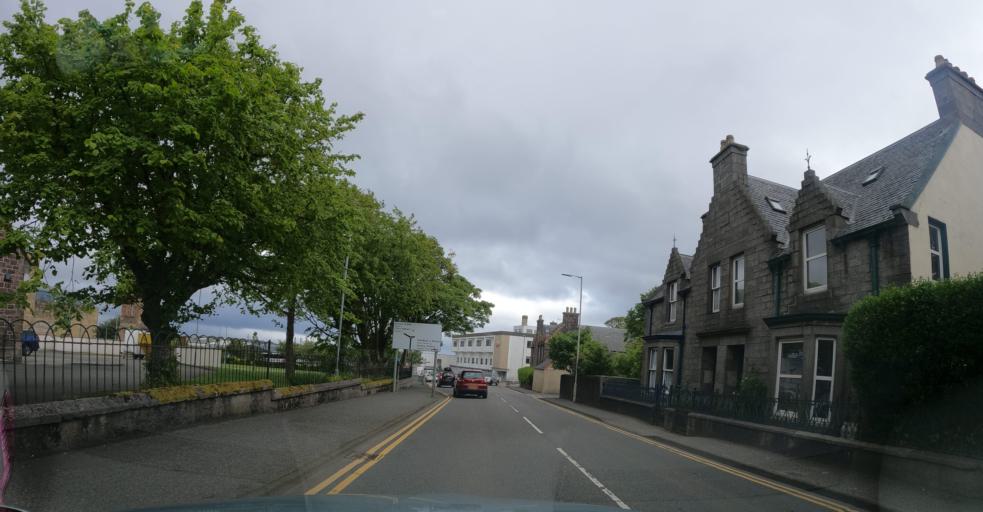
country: GB
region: Scotland
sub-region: Eilean Siar
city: Stornoway
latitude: 58.2092
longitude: -6.3818
